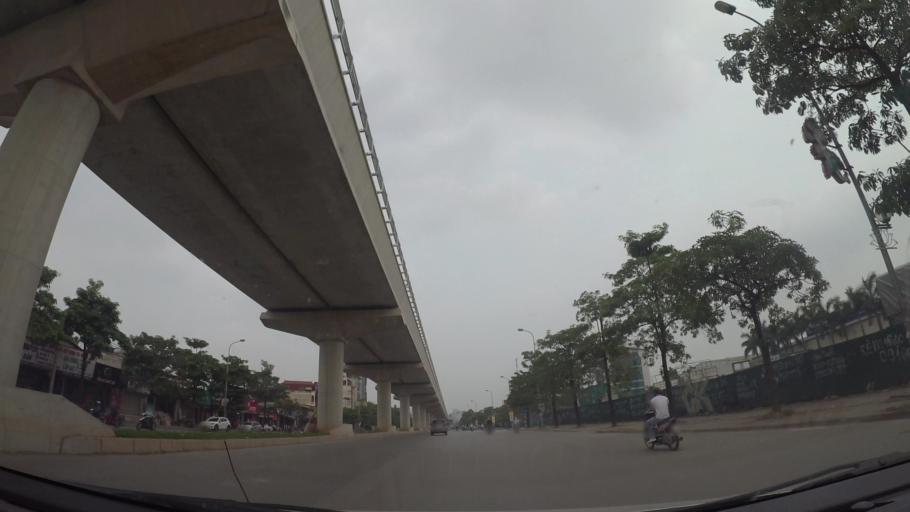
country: VN
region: Ha Noi
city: Cau Dien
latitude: 21.0501
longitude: 105.7392
